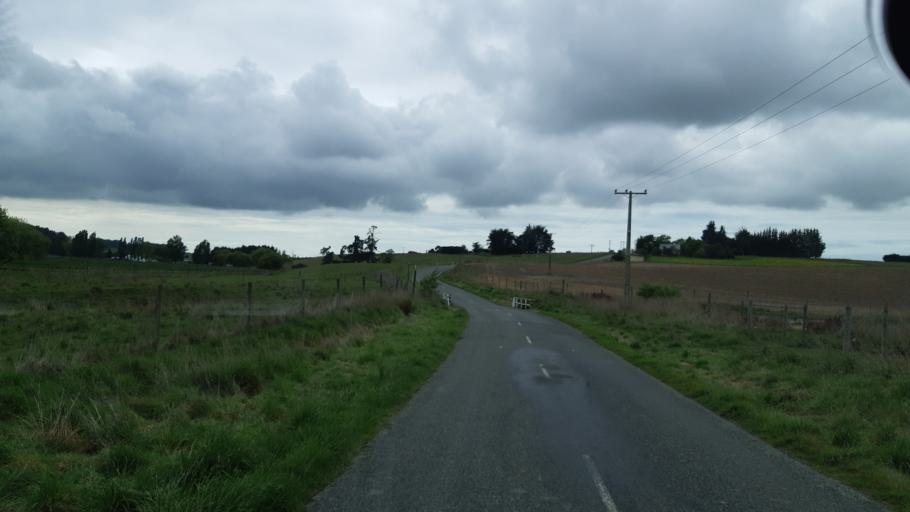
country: NZ
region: Canterbury
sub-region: Timaru District
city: Pleasant Point
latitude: -44.3295
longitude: 171.1518
